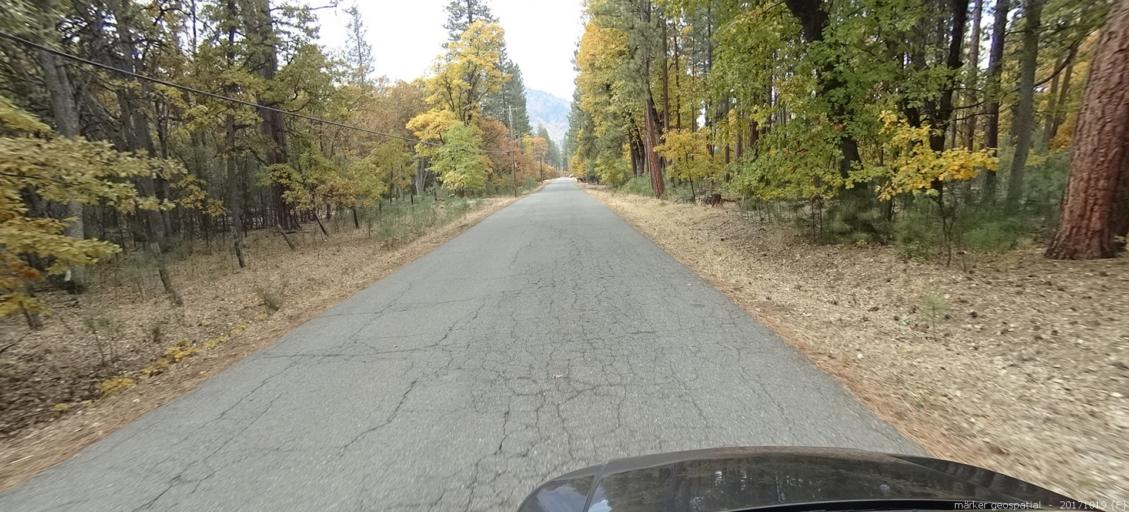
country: US
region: California
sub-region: Shasta County
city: Burney
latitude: 41.0799
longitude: -121.5217
